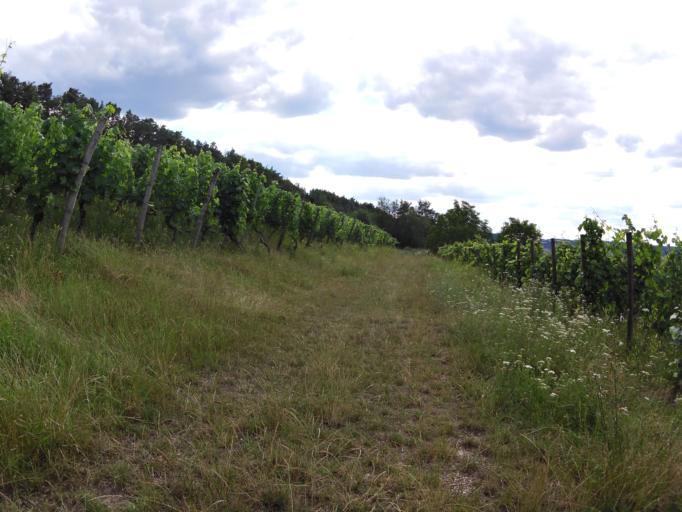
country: DE
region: Bavaria
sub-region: Regierungsbezirk Unterfranken
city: Thungersheim
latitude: 49.8864
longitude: 9.8609
